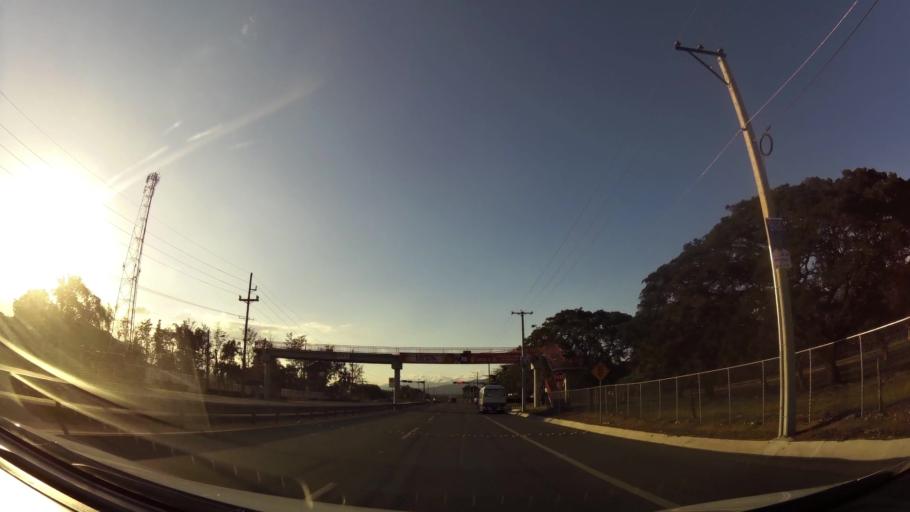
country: DO
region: Santiago
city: Palmar Arriba
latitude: 19.5111
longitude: -70.7579
